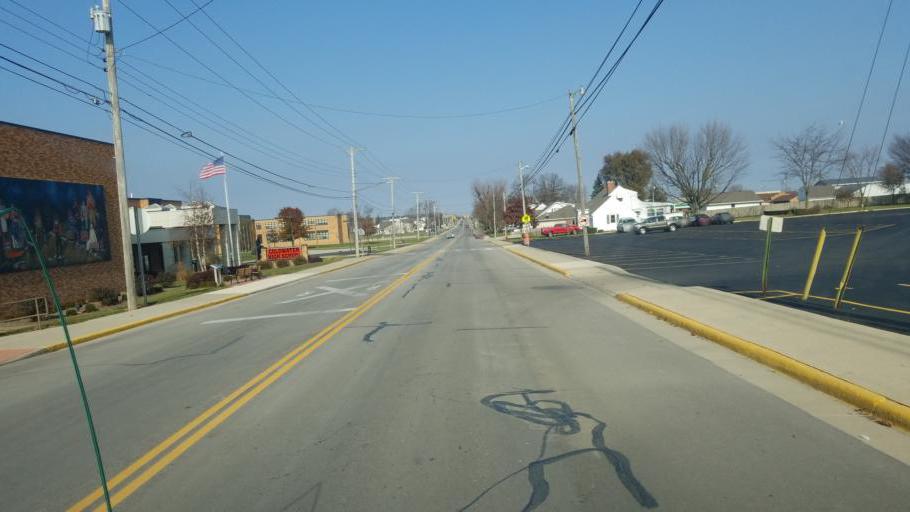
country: US
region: Ohio
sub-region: Mercer County
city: Coldwater
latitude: 40.4813
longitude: -84.6287
